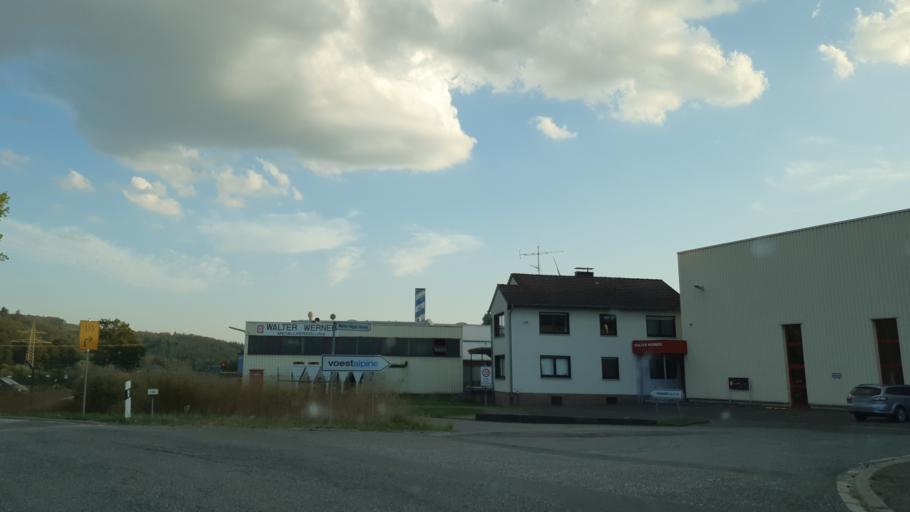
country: DE
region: Rheinland-Pfalz
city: Ellenberg
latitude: 49.6386
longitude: 7.1593
